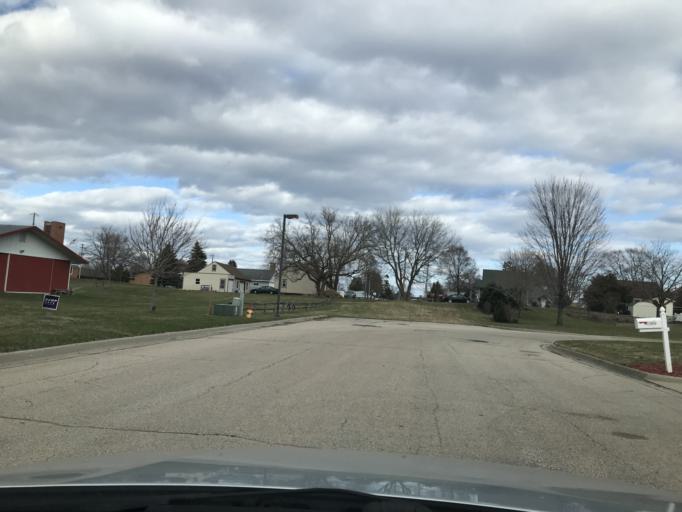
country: US
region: Michigan
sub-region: Menominee County
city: Menominee
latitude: 45.1226
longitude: -87.6260
